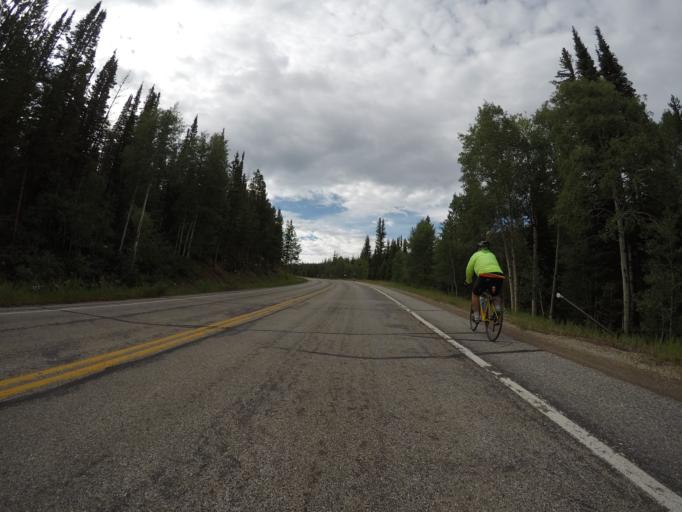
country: US
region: Wyoming
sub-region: Carbon County
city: Saratoga
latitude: 41.3349
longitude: -106.5205
